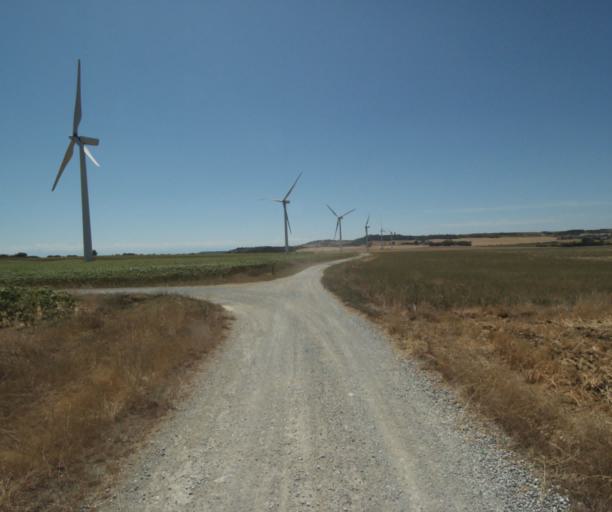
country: FR
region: Midi-Pyrenees
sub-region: Departement de la Haute-Garonne
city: Saint-Felix-Lauragais
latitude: 43.4629
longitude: 1.9182
